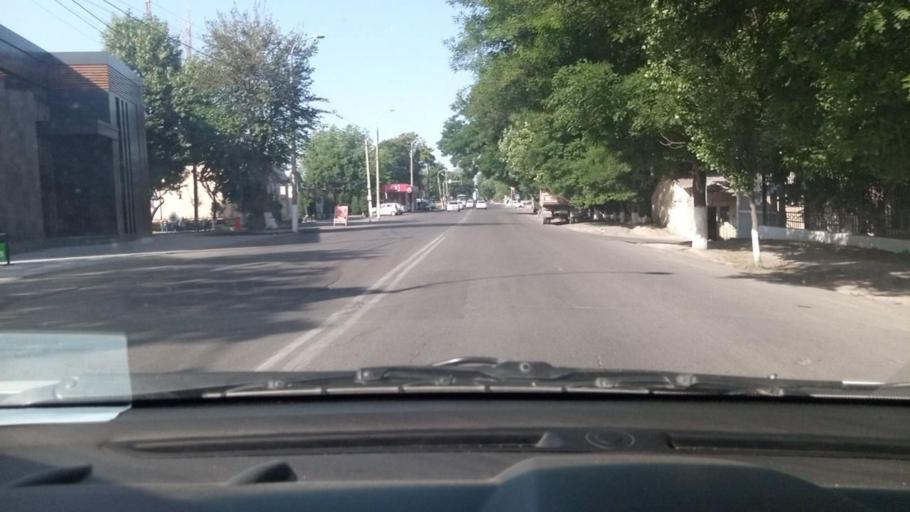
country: UZ
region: Toshkent
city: Salor
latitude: 41.3216
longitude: 69.3444
